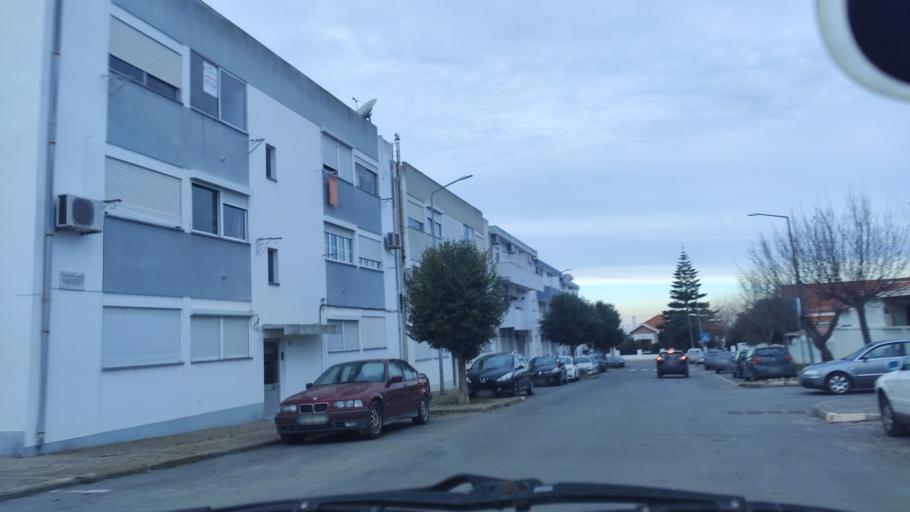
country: PT
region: Beja
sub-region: Beja
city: Ferreira do Alentejo
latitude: 38.0580
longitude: -8.1115
